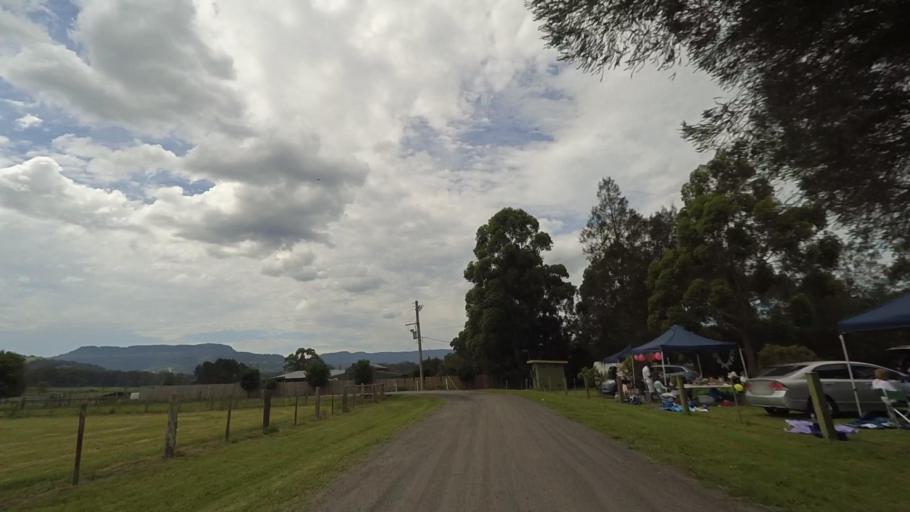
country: AU
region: New South Wales
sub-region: Shoalhaven Shire
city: Berry
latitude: -34.7931
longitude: 150.6745
